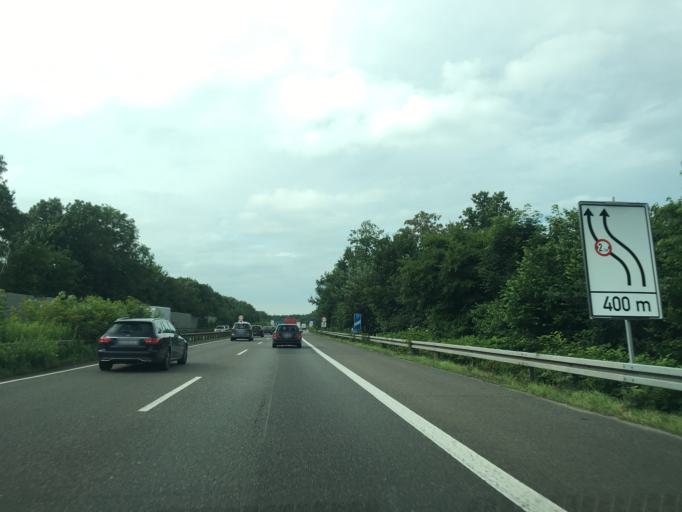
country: DE
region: North Rhine-Westphalia
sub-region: Regierungsbezirk Arnsberg
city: Herne
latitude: 51.5646
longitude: 7.1933
